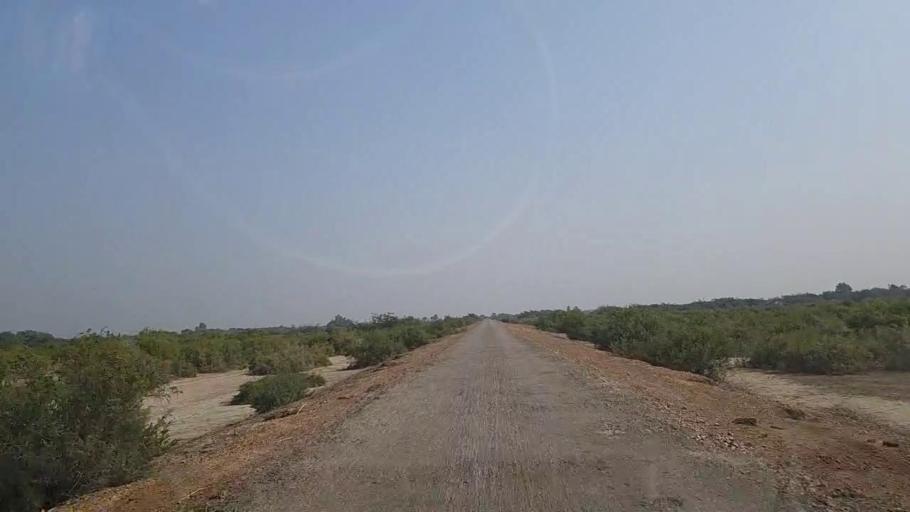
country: PK
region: Sindh
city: Keti Bandar
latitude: 24.2305
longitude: 67.6548
